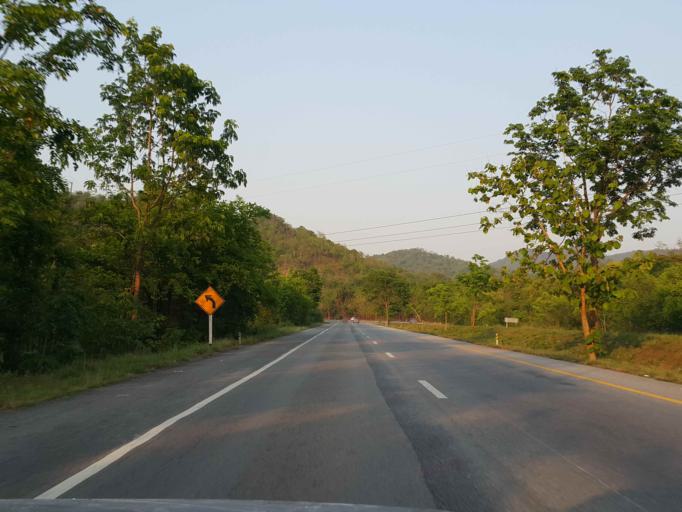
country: TH
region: Lampang
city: Sop Prap
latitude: 17.8156
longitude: 99.2781
